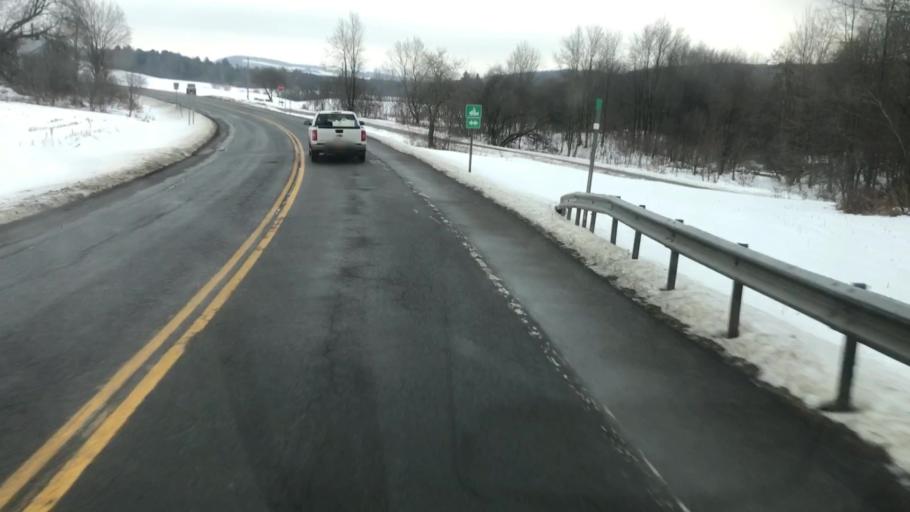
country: US
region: New York
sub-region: Tompkins County
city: Groton
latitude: 42.6824
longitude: -76.3009
